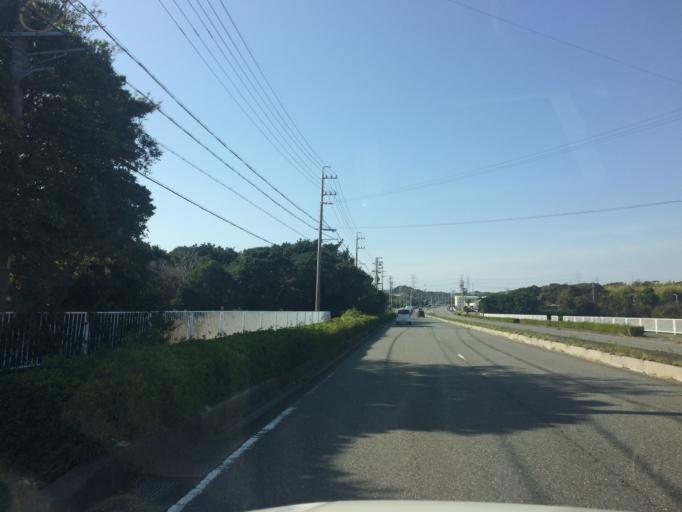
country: JP
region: Shizuoka
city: Oyama
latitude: 34.6233
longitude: 138.1674
